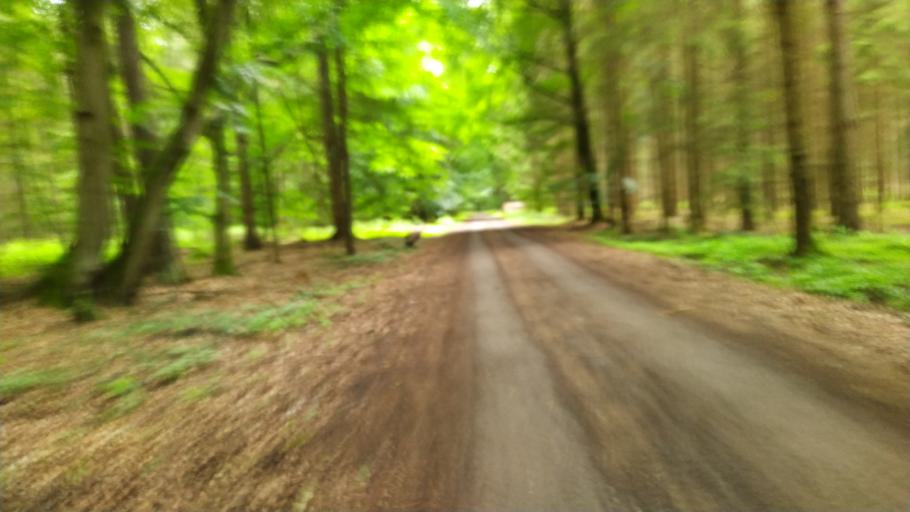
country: DE
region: Lower Saxony
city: Deinstedt
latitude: 53.4413
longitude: 9.1961
